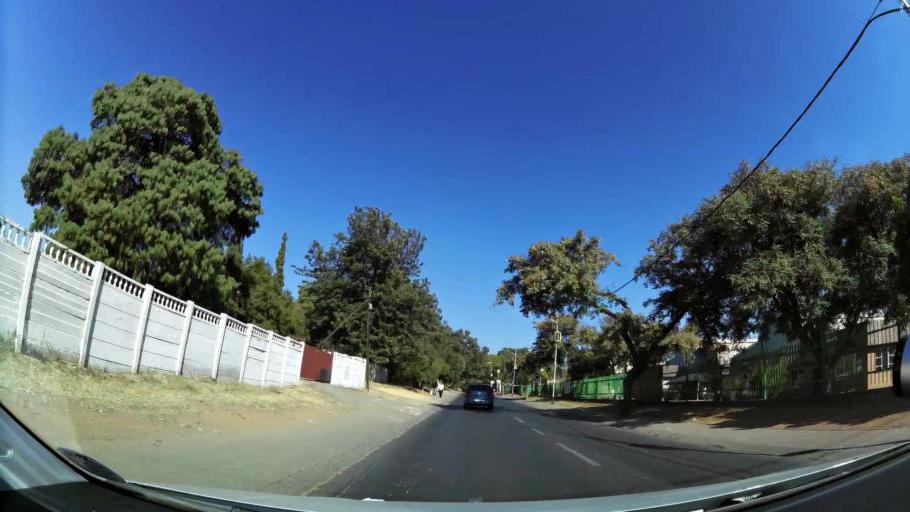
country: ZA
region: Gauteng
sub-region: City of Johannesburg Metropolitan Municipality
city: Modderfontein
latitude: -26.1170
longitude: 28.0991
